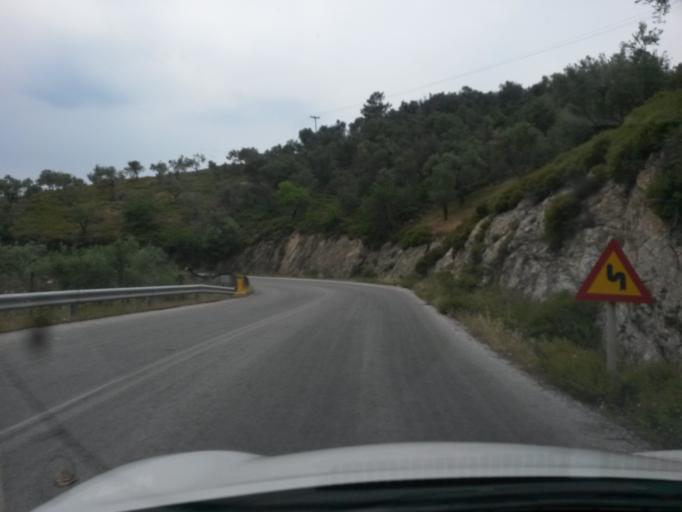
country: GR
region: North Aegean
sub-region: Nomos Lesvou
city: Skopelos
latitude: 39.0158
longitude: 26.4643
